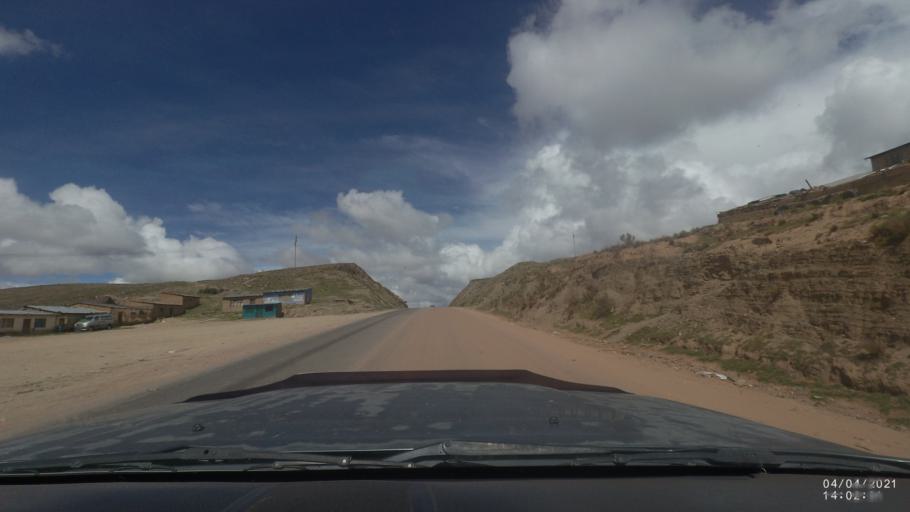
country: BO
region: Cochabamba
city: Colchani
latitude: -17.6804
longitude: -66.7302
